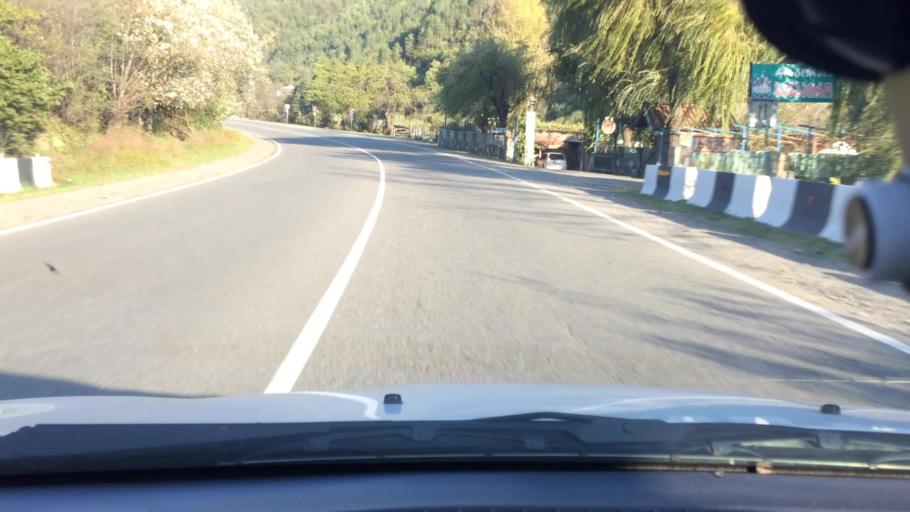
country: GE
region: Imereti
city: Kharagauli
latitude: 42.1075
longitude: 43.3392
